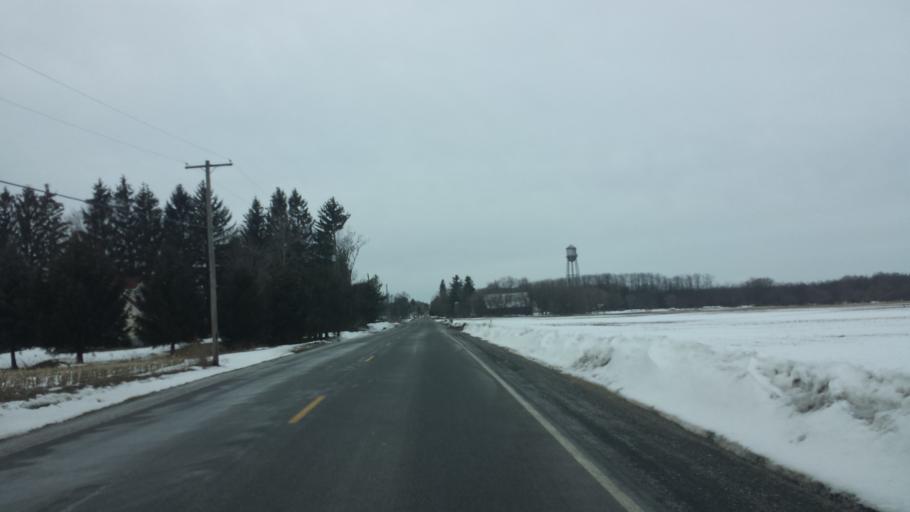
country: US
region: New York
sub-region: Tompkins County
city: Northwest Ithaca
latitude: 42.4962
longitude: -76.5866
